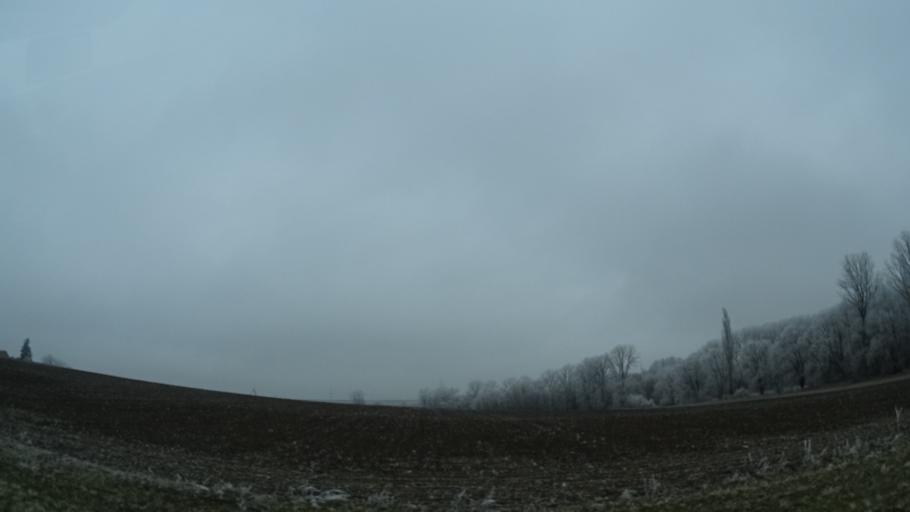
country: DE
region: Bavaria
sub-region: Regierungsbezirk Unterfranken
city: Butthard
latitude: 49.6058
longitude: 9.9139
